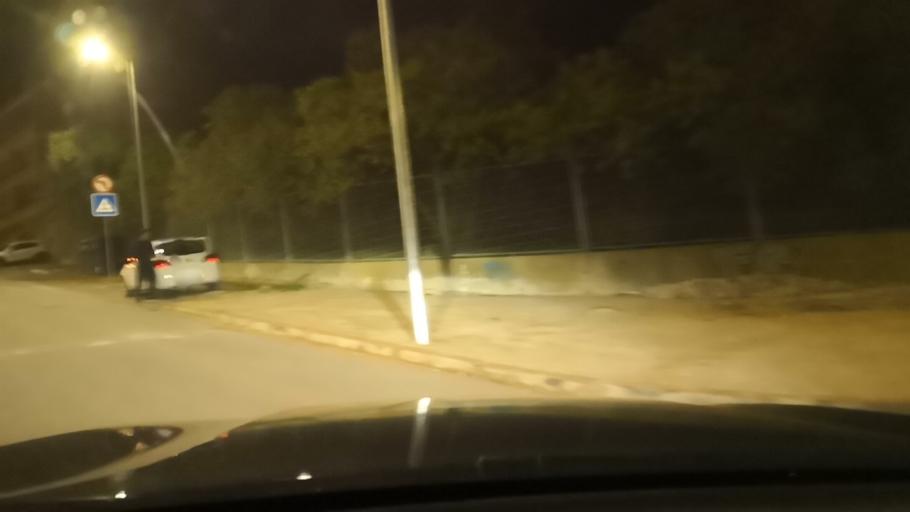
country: PT
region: Setubal
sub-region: Setubal
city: Setubal
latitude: 38.5294
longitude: -8.9030
